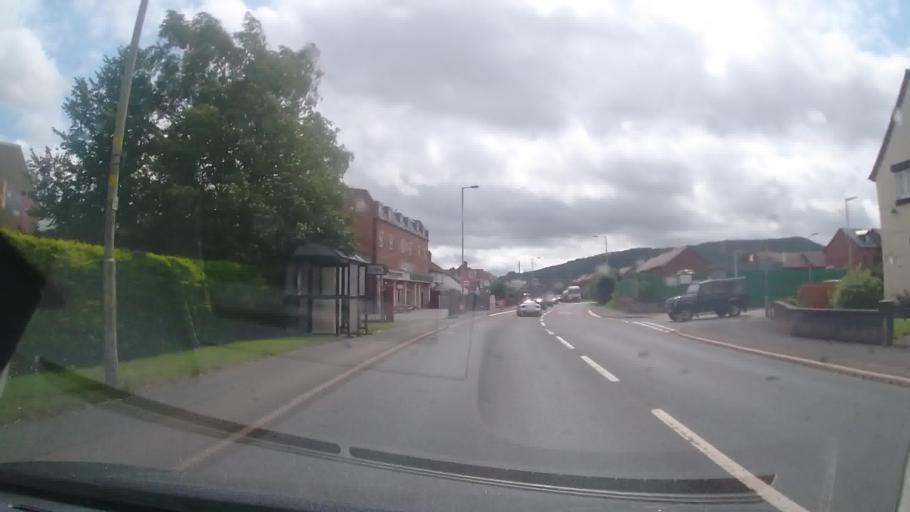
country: GB
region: England
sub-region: Shropshire
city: Craven Arms
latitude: 52.4432
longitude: -2.8360
